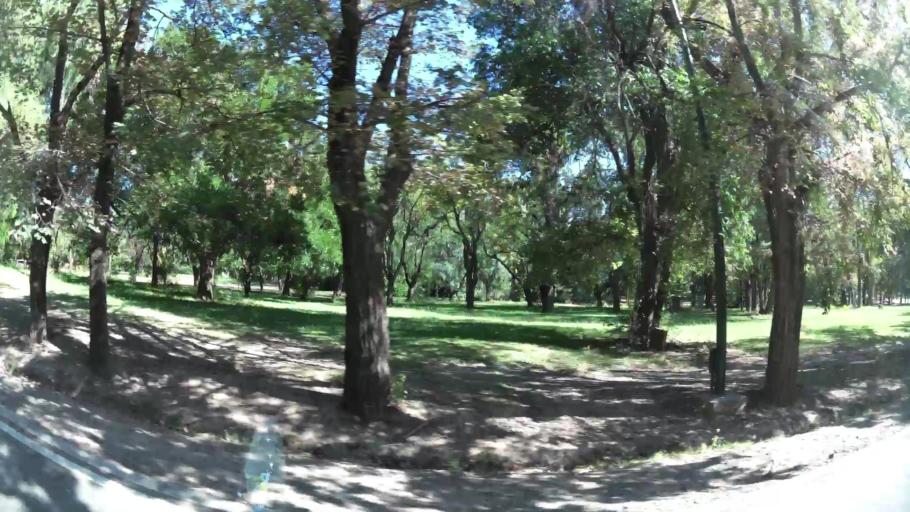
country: AR
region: Mendoza
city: Mendoza
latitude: -32.8891
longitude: -68.8722
